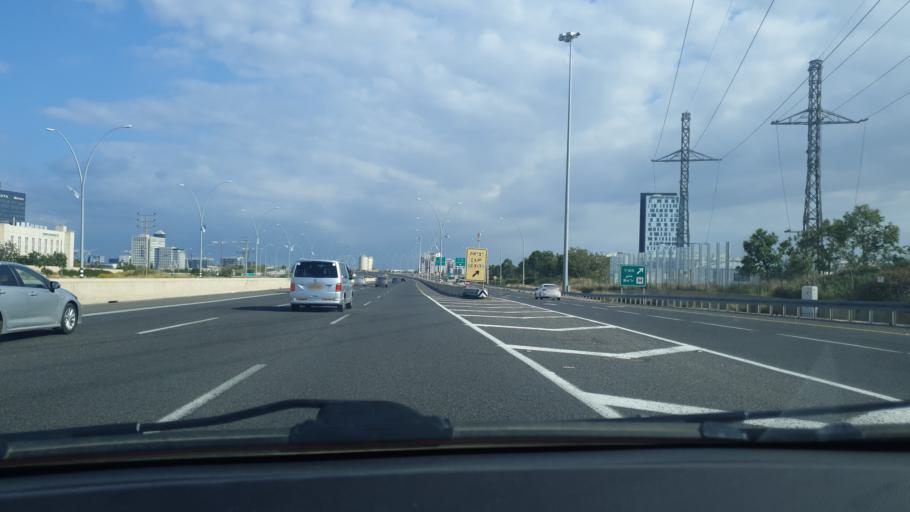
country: IL
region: Central District
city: Ra'anana
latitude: 32.1868
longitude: 34.8900
